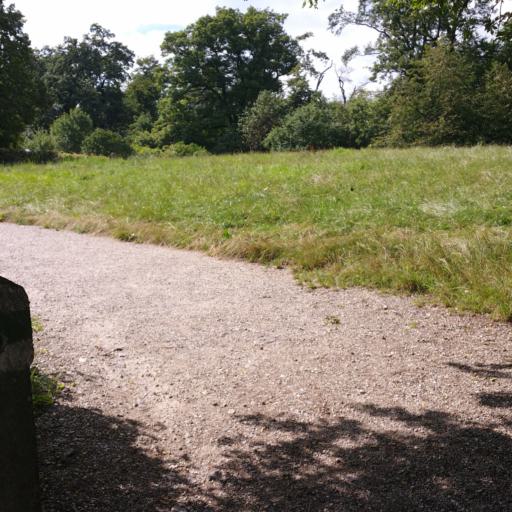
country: AT
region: Lower Austria
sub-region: Politischer Bezirk Wien-Umgebung
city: Purkersdorf
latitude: 48.2214
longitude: 16.2672
